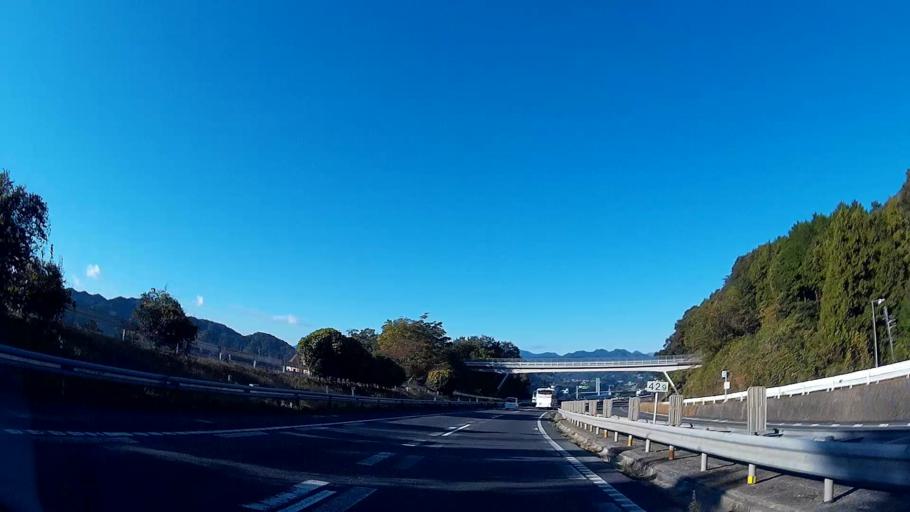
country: JP
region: Yamanashi
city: Uenohara
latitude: 35.6188
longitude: 139.1919
